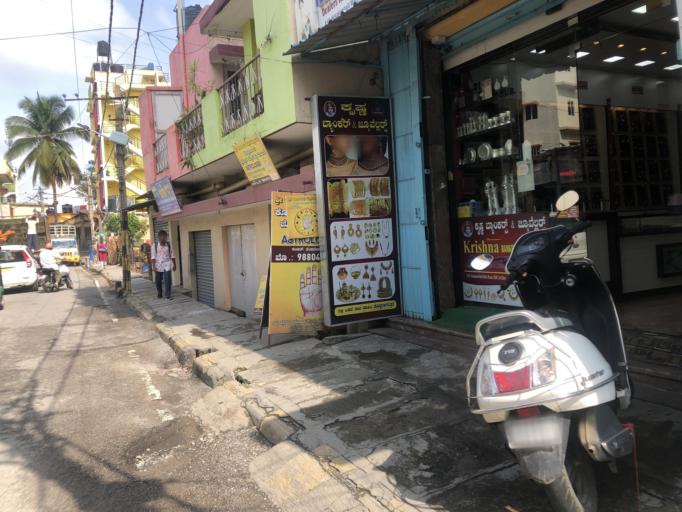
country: IN
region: Karnataka
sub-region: Bangalore Urban
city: Bangalore
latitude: 12.9297
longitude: 77.5378
